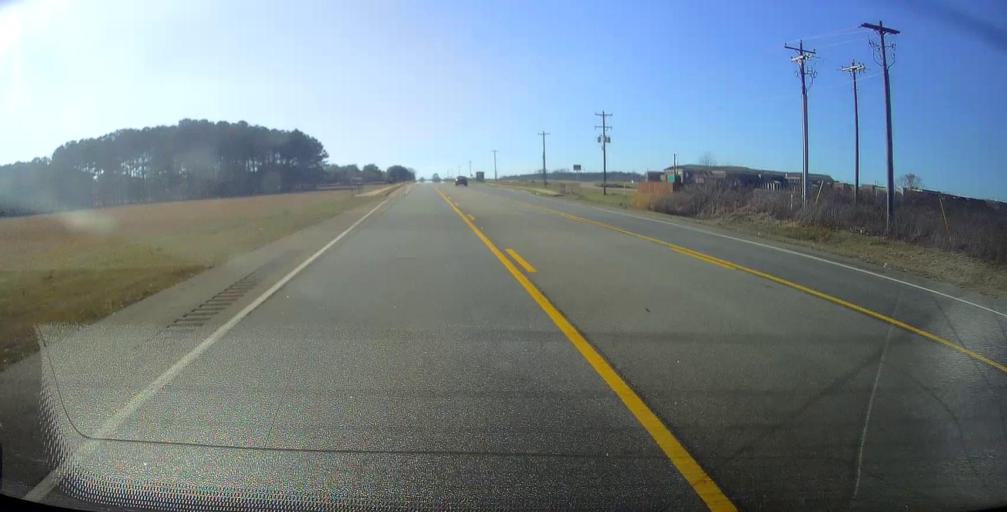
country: US
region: Georgia
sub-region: Sumter County
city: Americus
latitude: 32.1188
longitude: -84.1818
